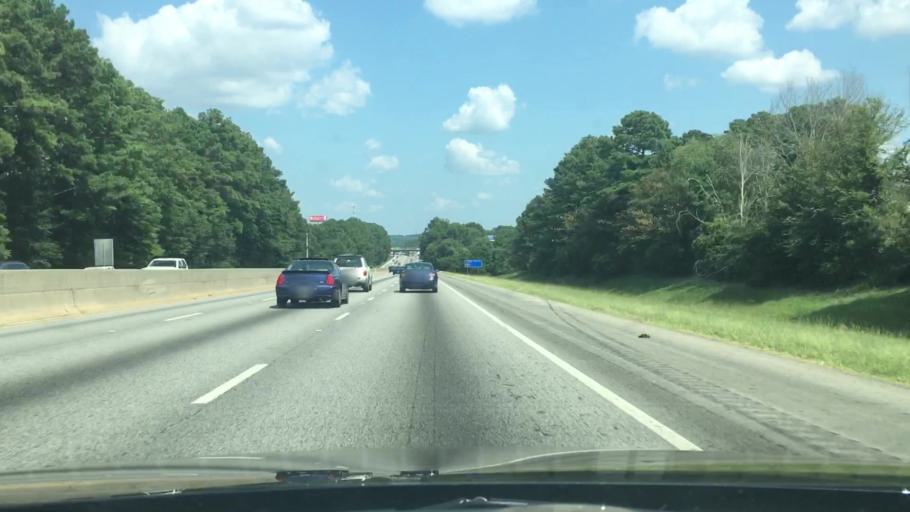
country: US
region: Georgia
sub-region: DeKalb County
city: Redan
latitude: 33.7032
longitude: -84.1577
